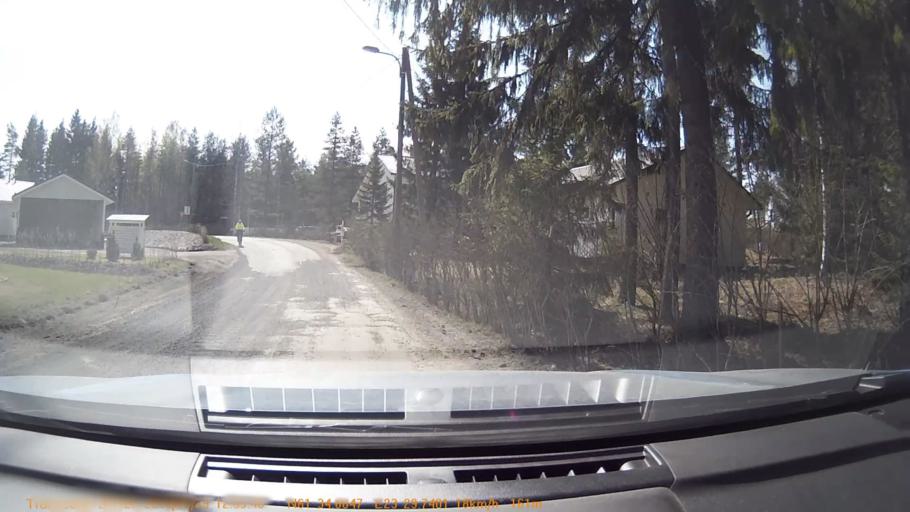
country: FI
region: Pirkanmaa
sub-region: Tampere
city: Yloejaervi
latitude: 61.5767
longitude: 23.4957
